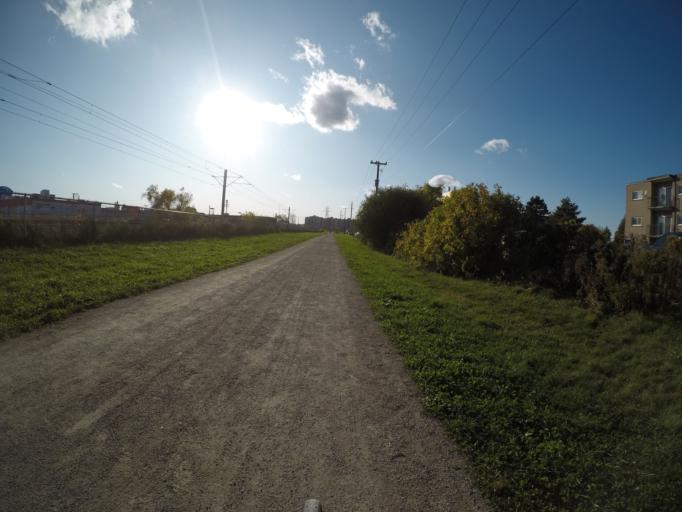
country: CA
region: Ontario
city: Kitchener
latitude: 43.4205
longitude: -80.4513
